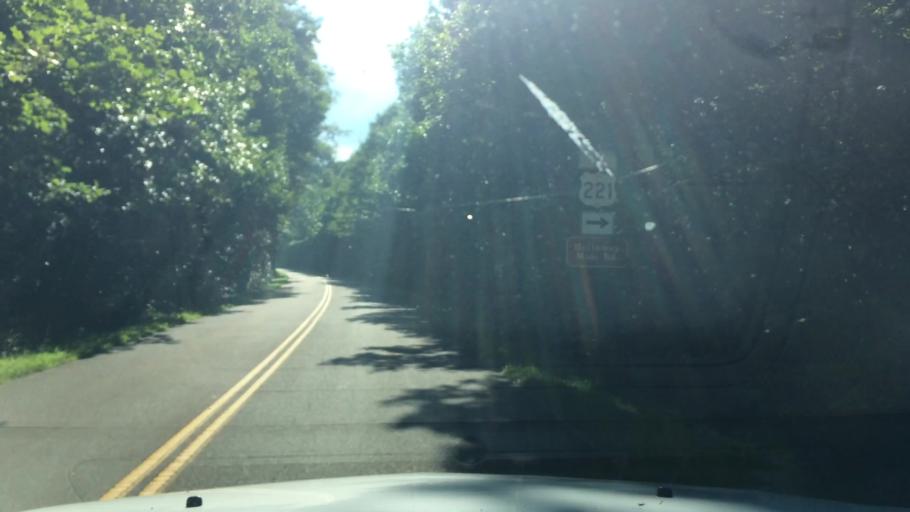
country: US
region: North Carolina
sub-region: Watauga County
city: Foscoe
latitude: 36.1322
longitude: -81.7579
